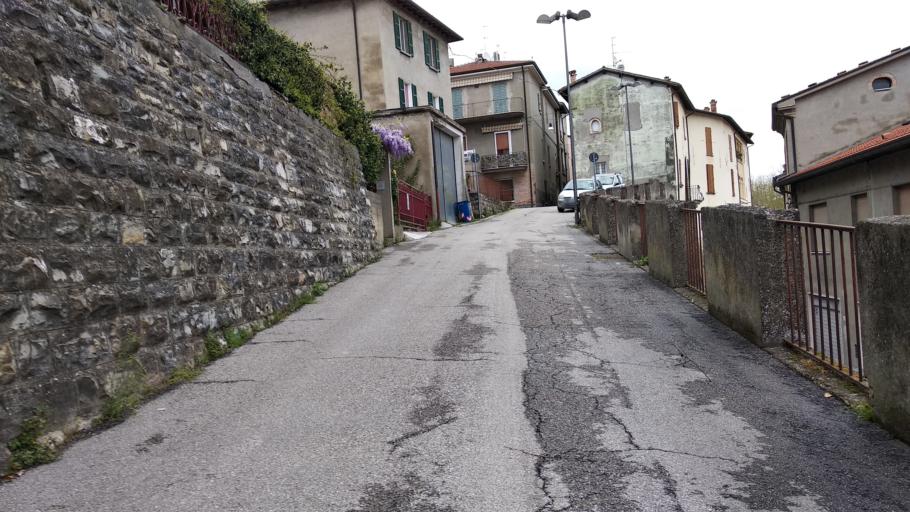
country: IT
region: Emilia-Romagna
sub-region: Forli-Cesena
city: Castrocaro Terme
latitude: 44.1702
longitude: 11.9447
